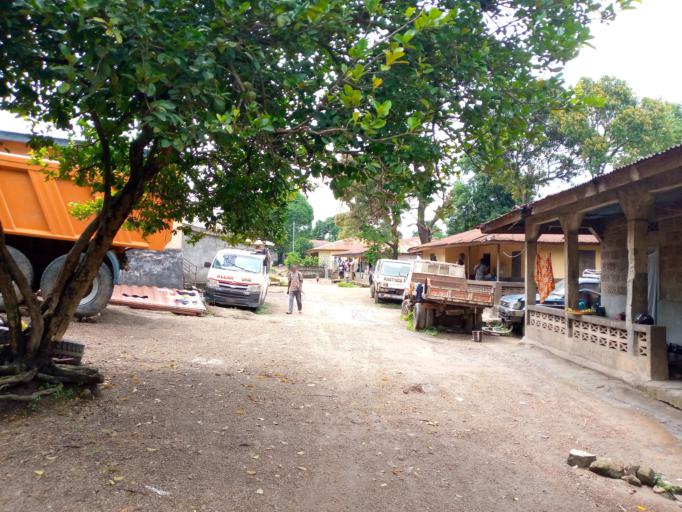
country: SL
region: Northern Province
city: Magburaka
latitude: 8.7182
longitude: -11.9394
